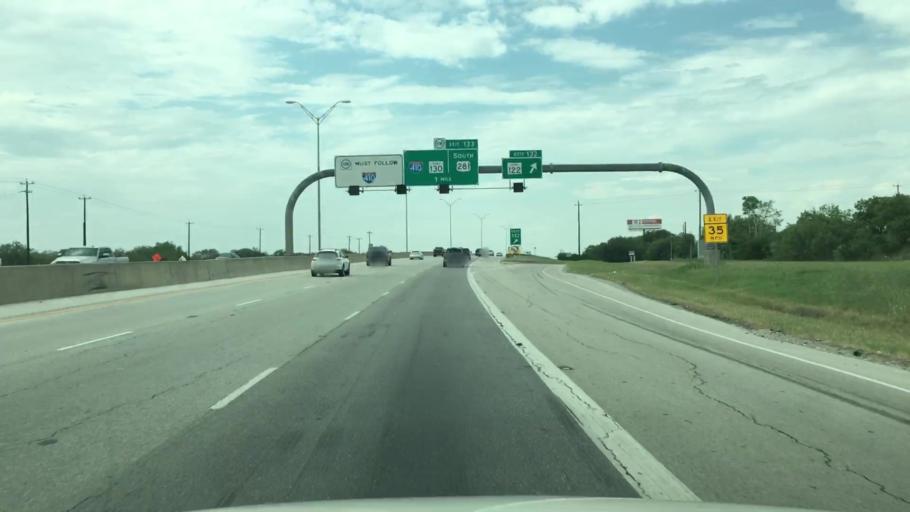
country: US
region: Texas
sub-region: Bexar County
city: Elmendorf
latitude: 29.3130
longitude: -98.4046
